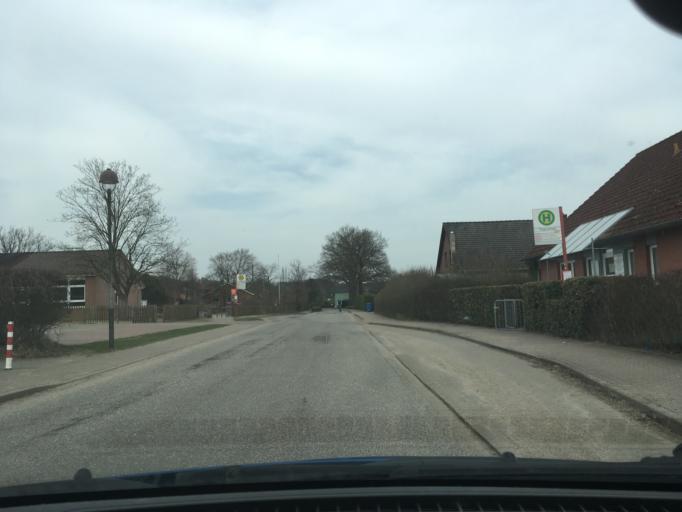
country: DE
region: Lower Saxony
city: Tespe
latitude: 53.3942
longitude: 10.4147
